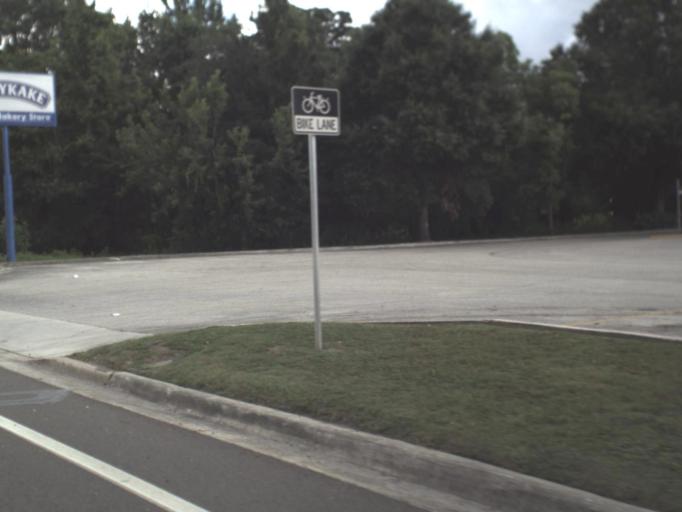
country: US
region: Florida
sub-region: Duval County
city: Jacksonville
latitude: 30.3654
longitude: -81.7199
